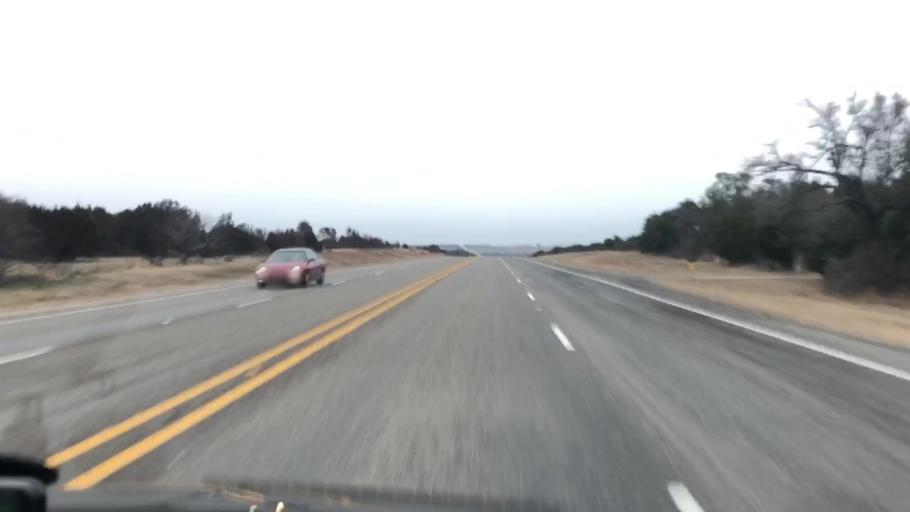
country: US
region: Texas
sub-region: Lampasas County
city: Lampasas
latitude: 31.1923
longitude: -98.1718
